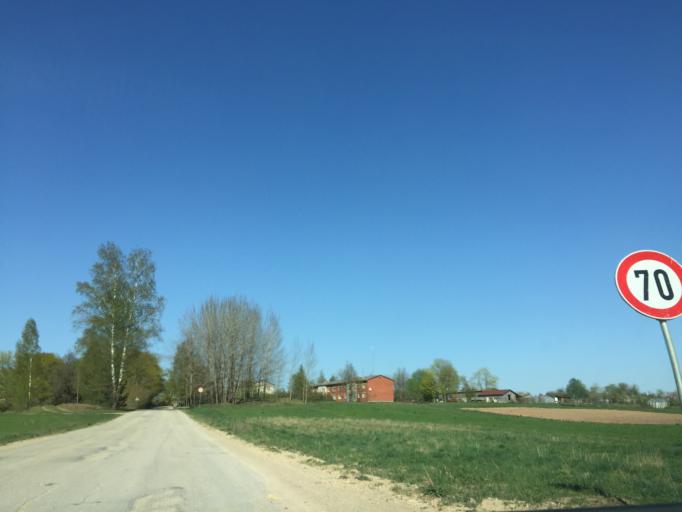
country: LV
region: Skriveri
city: Skriveri
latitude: 56.8340
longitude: 25.2272
